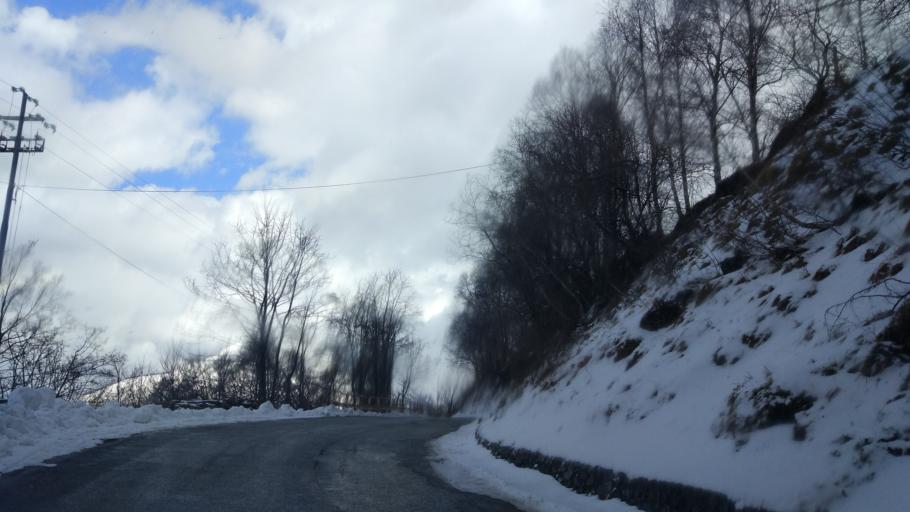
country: IT
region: Lombardy
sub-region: Provincia di Lecco
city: Moggio
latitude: 45.9030
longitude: 9.4949
